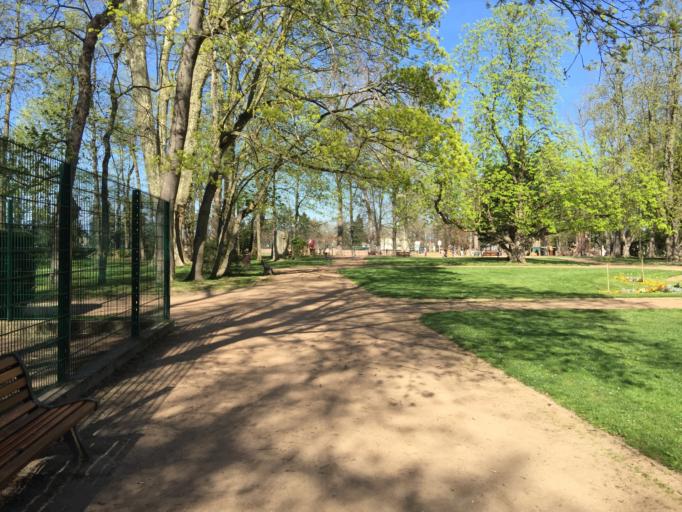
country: FR
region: Rhone-Alpes
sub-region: Departement de la Loire
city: Feurs
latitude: 45.7408
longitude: 4.2229
